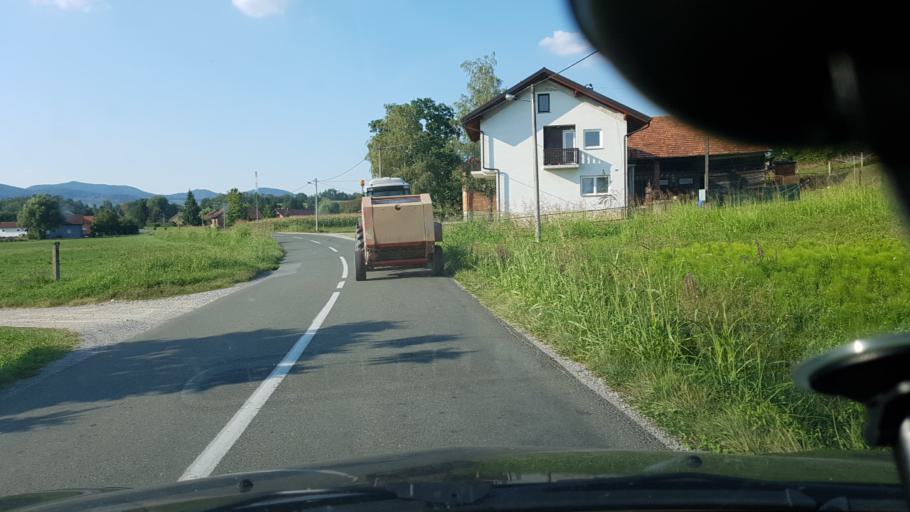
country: SI
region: Bistrica ob Sotli
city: Bistrica ob Sotli
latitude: 45.9938
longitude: 15.7229
